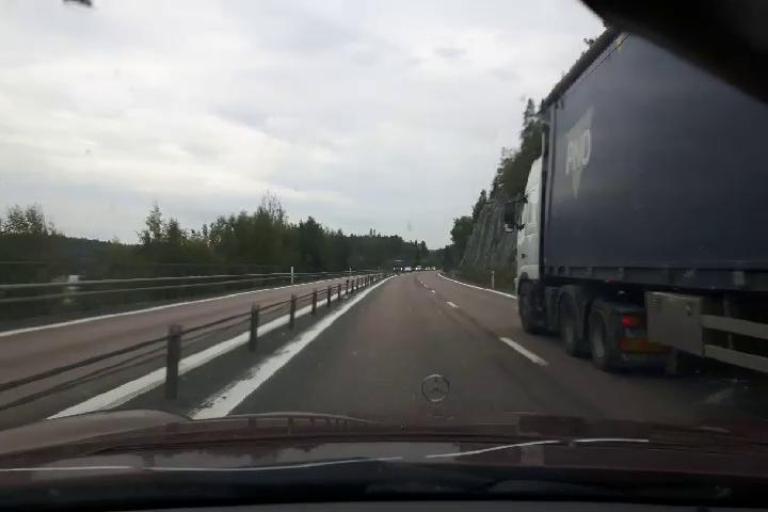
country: SE
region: Vaesternorrland
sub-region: Haernoesands Kommun
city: Haernoesand
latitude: 62.8200
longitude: 17.9697
